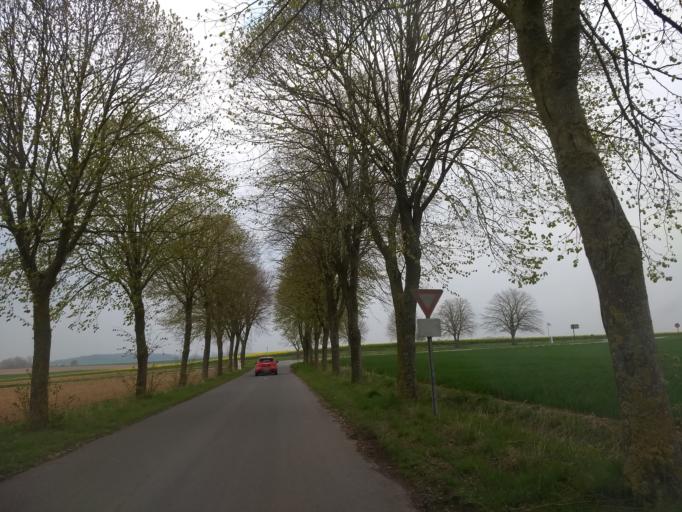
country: FR
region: Nord-Pas-de-Calais
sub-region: Departement du Pas-de-Calais
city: Maroeuil
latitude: 50.3377
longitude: 2.7040
